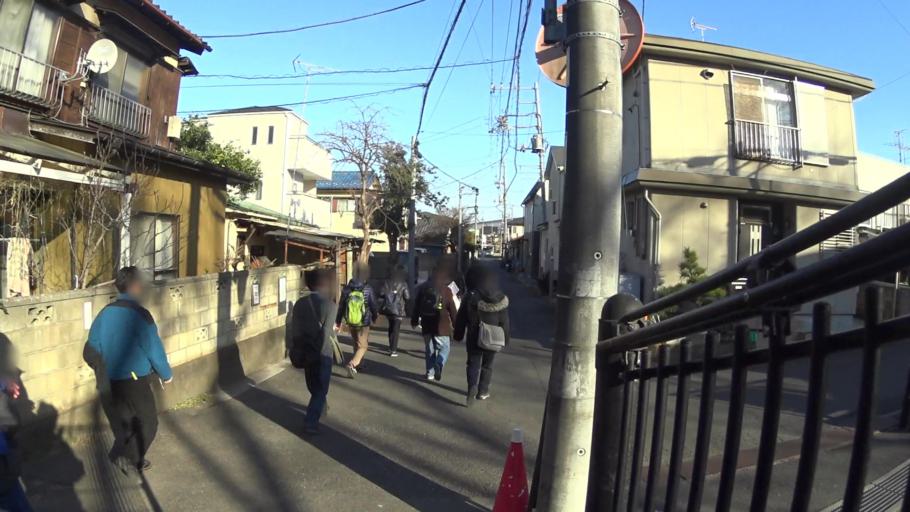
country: JP
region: Saitama
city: Shimotoda
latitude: 35.8454
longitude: 139.6896
